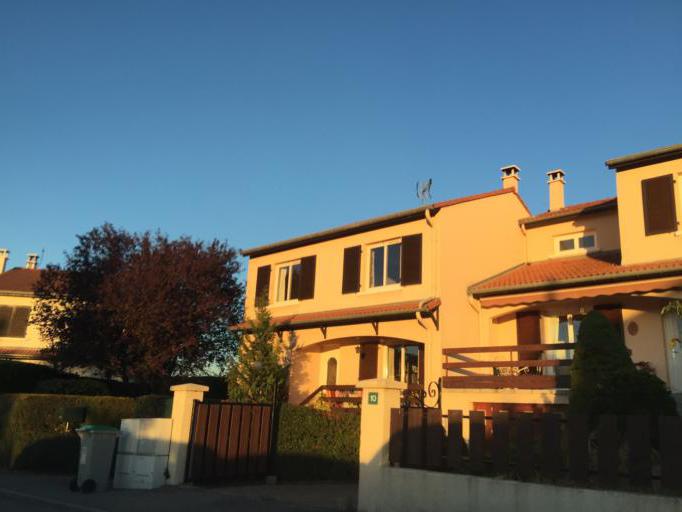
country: FR
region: Rhone-Alpes
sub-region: Departement de la Loire
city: Saint-Chamond
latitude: 45.4895
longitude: 4.5319
